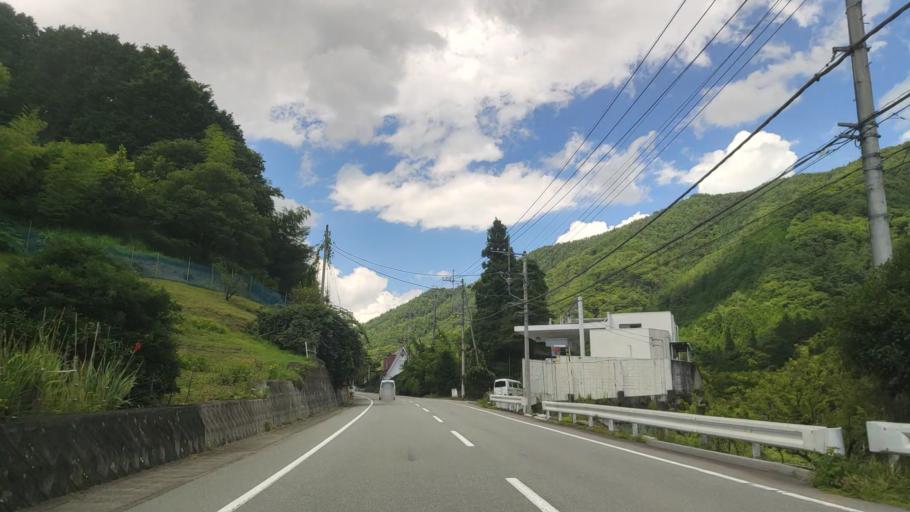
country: JP
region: Yamanashi
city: Enzan
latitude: 35.7738
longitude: 138.7385
